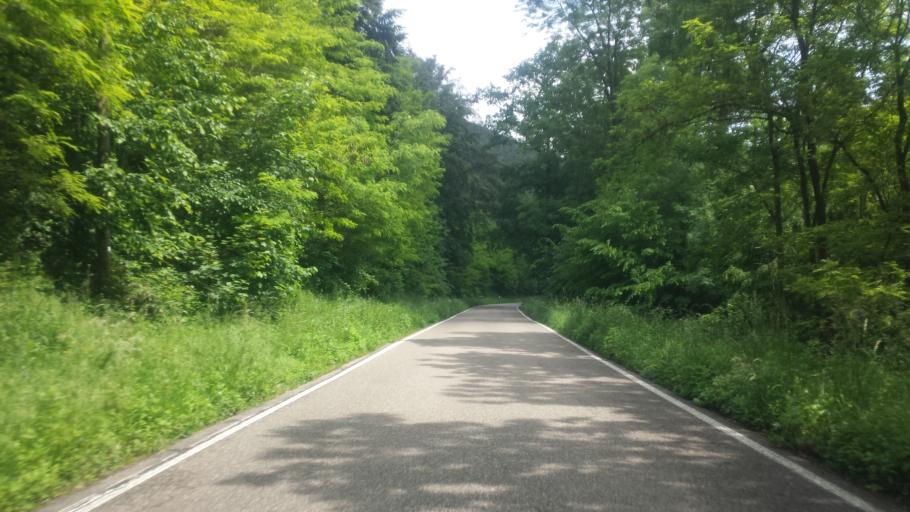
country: DE
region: Rheinland-Pfalz
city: Wachenheim
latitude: 49.4309
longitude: 8.1479
